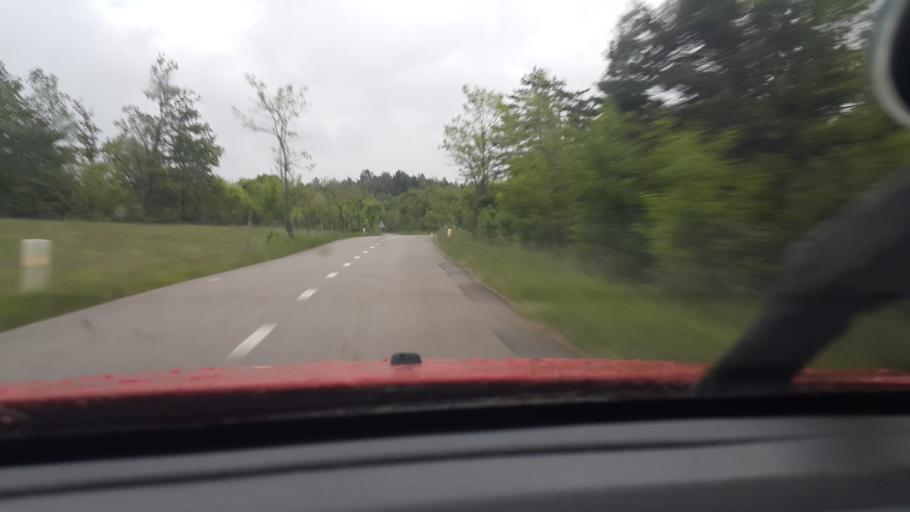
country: SI
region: Sezana
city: Sezana
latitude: 45.7756
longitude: 13.8712
